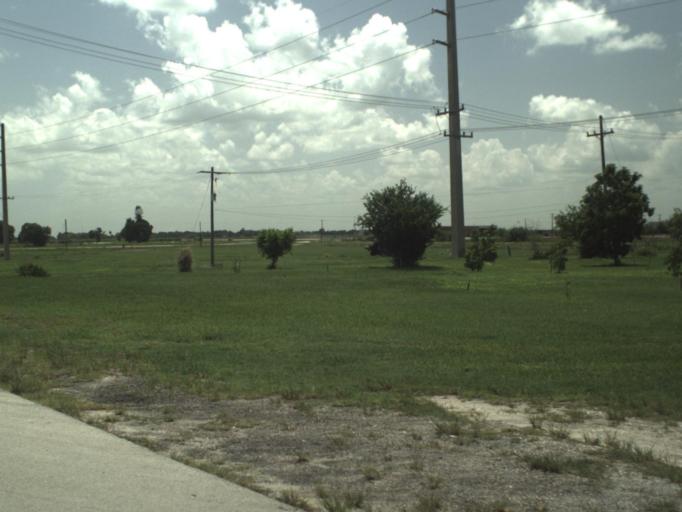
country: US
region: Florida
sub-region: Palm Beach County
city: Belle Glade
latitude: 26.7190
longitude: -80.6682
